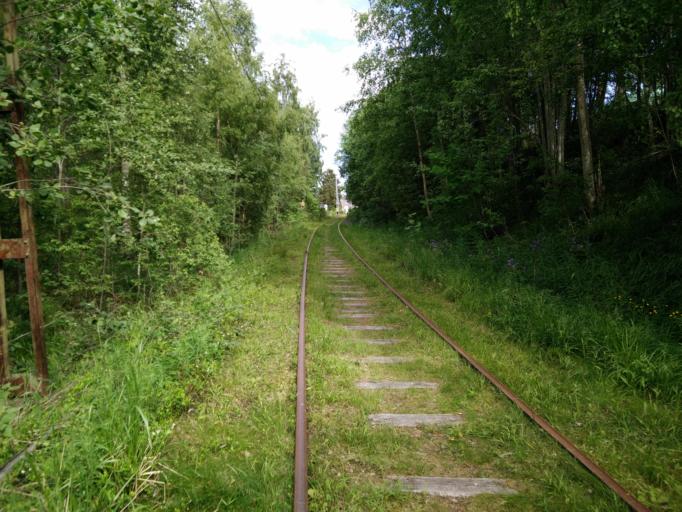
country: SE
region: Gaevleborg
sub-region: Hudiksvalls Kommun
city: Delsbo
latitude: 61.7982
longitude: 16.5455
